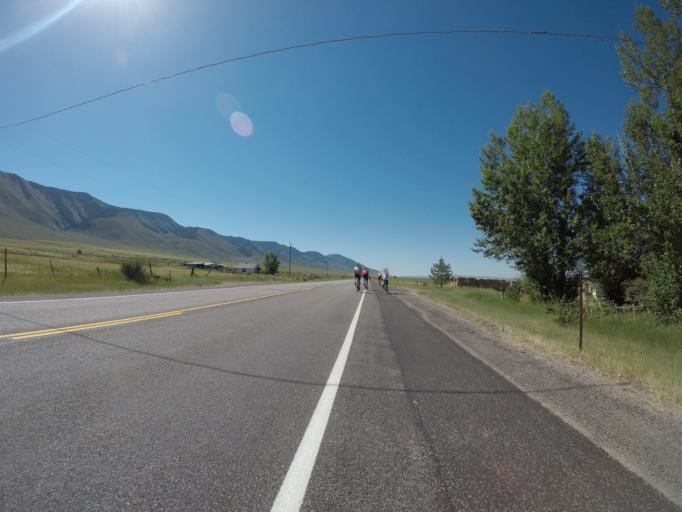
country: US
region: Idaho
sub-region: Bear Lake County
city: Montpelier
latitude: 42.3573
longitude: -111.0495
